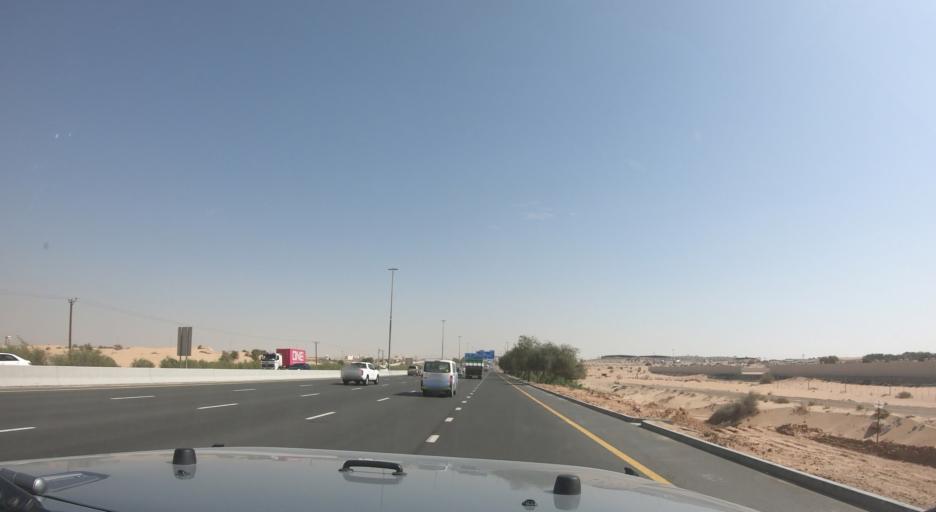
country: AE
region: Ash Shariqah
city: Sharjah
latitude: 25.1647
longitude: 55.4770
